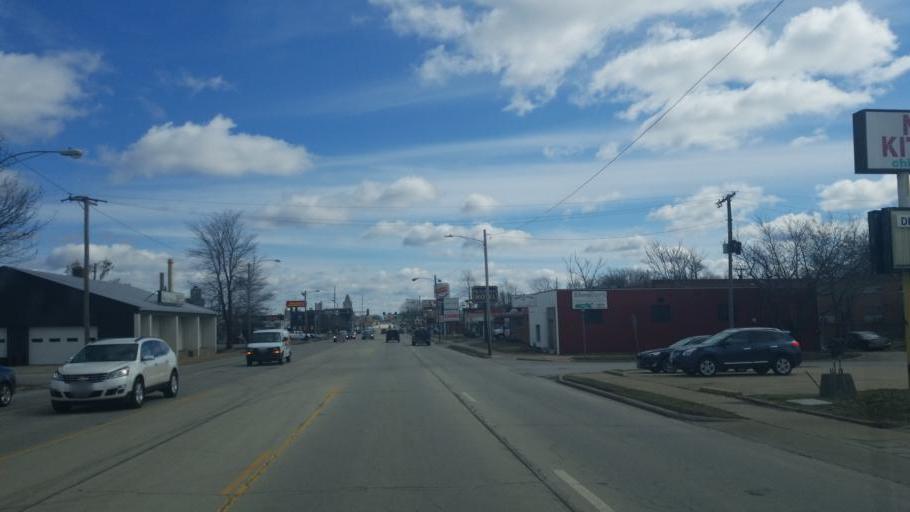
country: US
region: Illinois
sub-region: Macon County
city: Decatur
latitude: 39.8460
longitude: -88.9439
